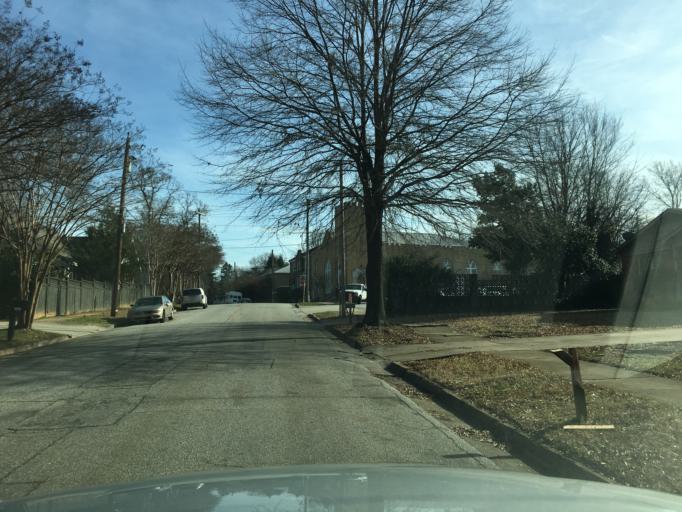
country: US
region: South Carolina
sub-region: Greenville County
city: Greenville
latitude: 34.8582
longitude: -82.4072
